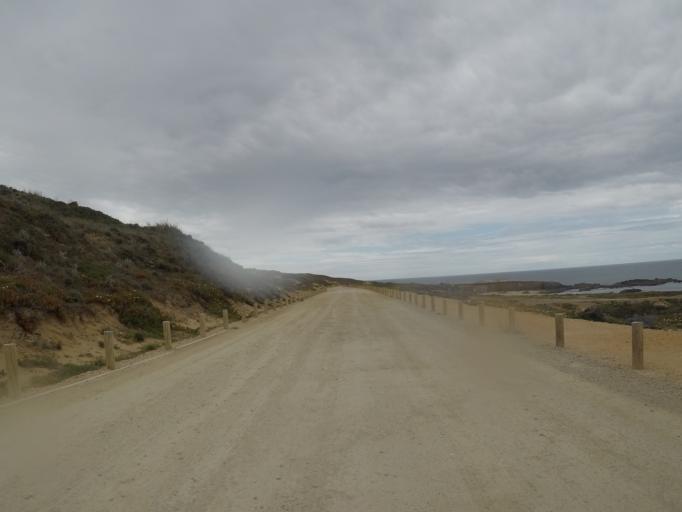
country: PT
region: Beja
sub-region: Odemira
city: Vila Nova de Milfontes
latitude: 37.6507
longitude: -8.8020
